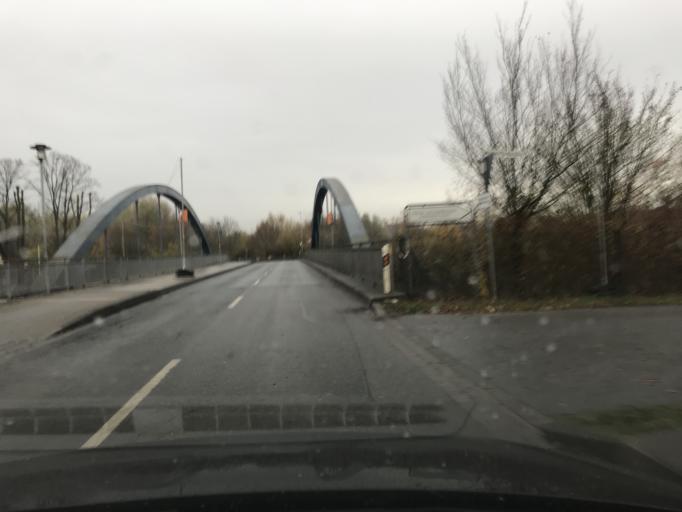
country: DE
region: North Rhine-Westphalia
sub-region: Regierungsbezirk Arnsberg
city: Hamm
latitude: 51.6933
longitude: 7.8406
